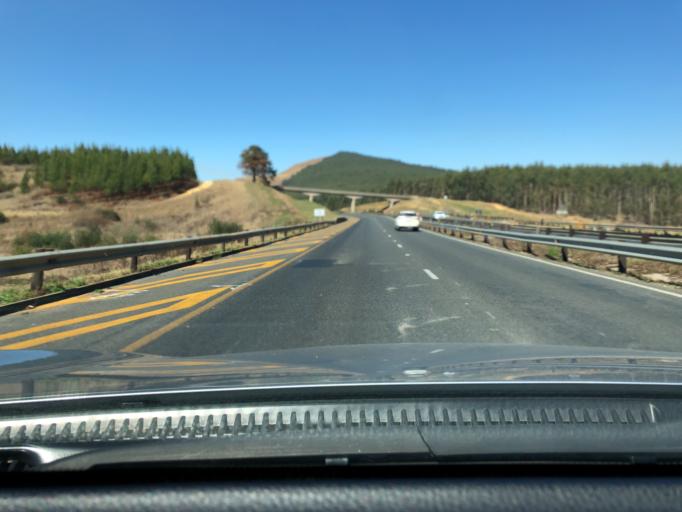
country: ZA
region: KwaZulu-Natal
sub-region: uMgungundlovu District Municipality
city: Howick
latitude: -29.4069
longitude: 30.1442
